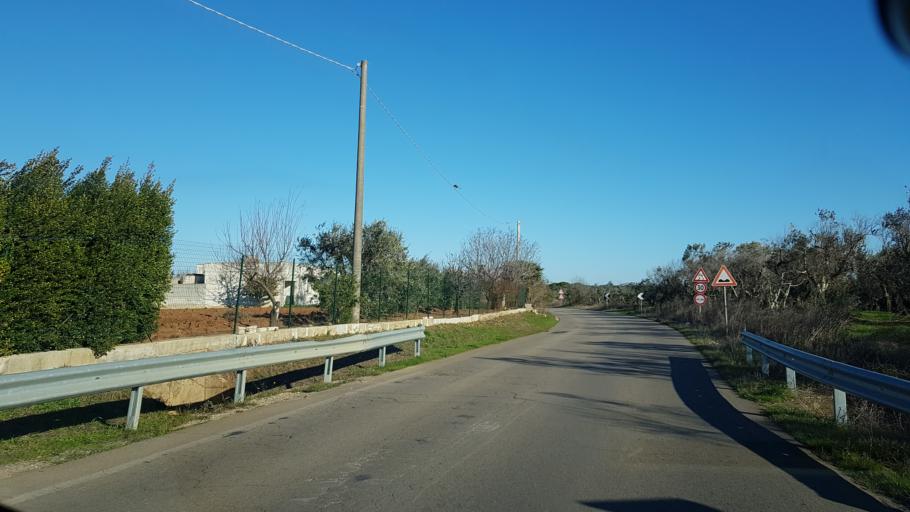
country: IT
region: Apulia
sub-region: Provincia di Lecce
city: Melissano
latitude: 39.9966
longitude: 18.1273
